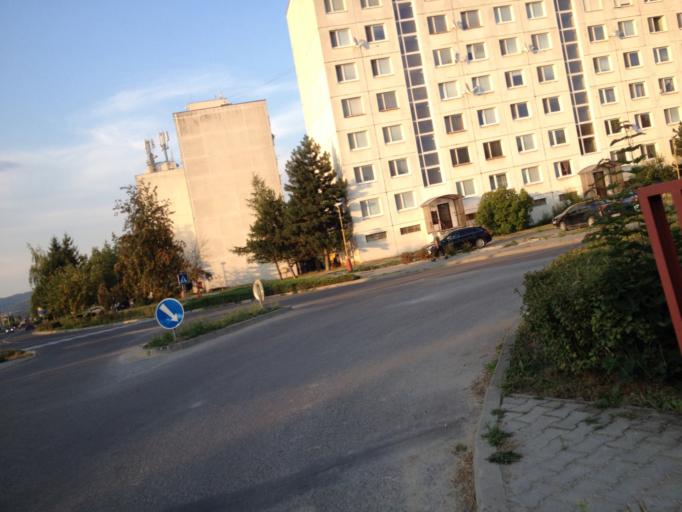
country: SK
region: Nitriansky
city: Puchov
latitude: 49.0605
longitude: 18.3221
